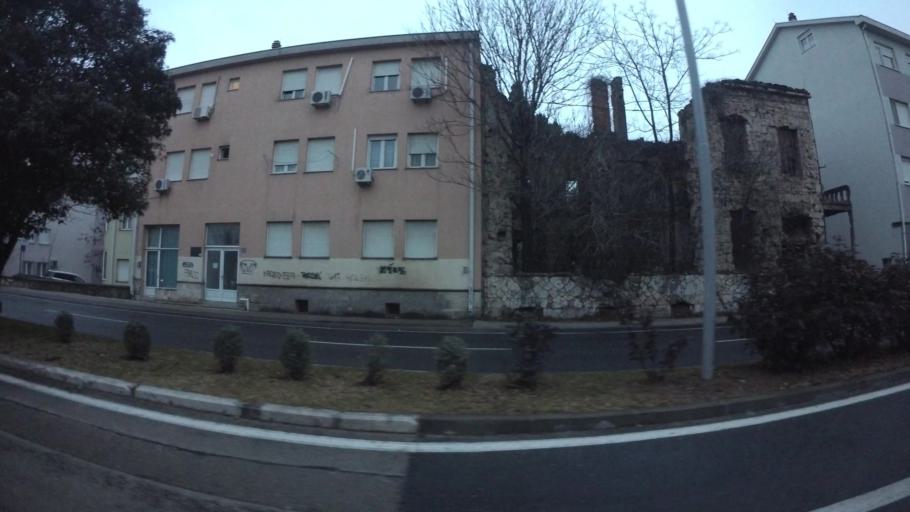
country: BA
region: Federation of Bosnia and Herzegovina
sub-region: Hercegovacko-Bosanski Kanton
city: Mostar
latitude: 43.3404
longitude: 17.8085
